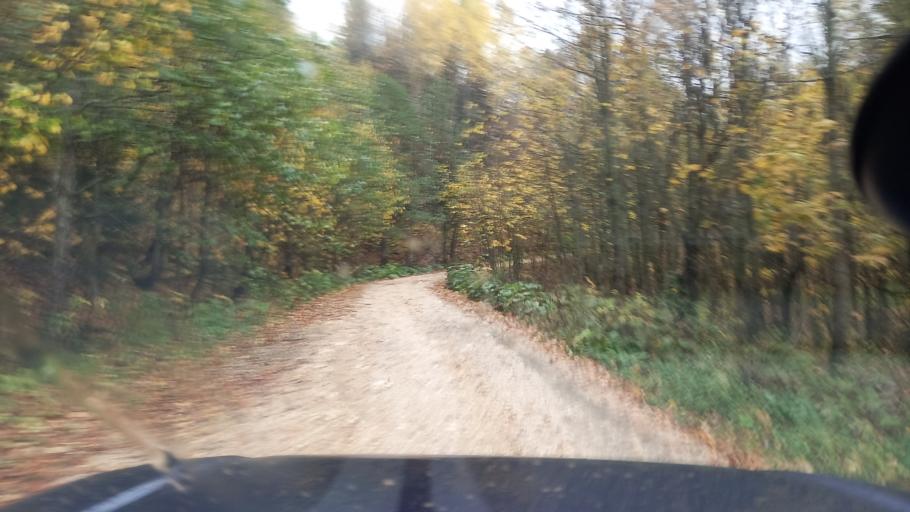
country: RU
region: Krasnodarskiy
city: Neftegorsk
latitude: 44.0148
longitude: 39.8441
